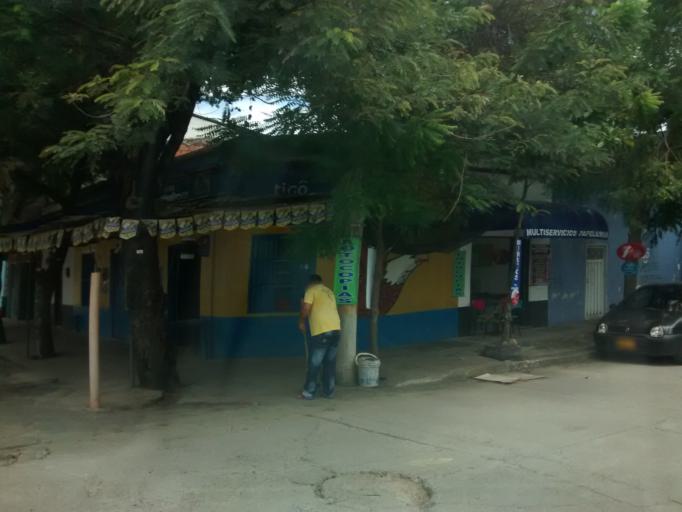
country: CO
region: Cundinamarca
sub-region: Girardot
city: Girardot City
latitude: 4.3084
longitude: -74.8041
